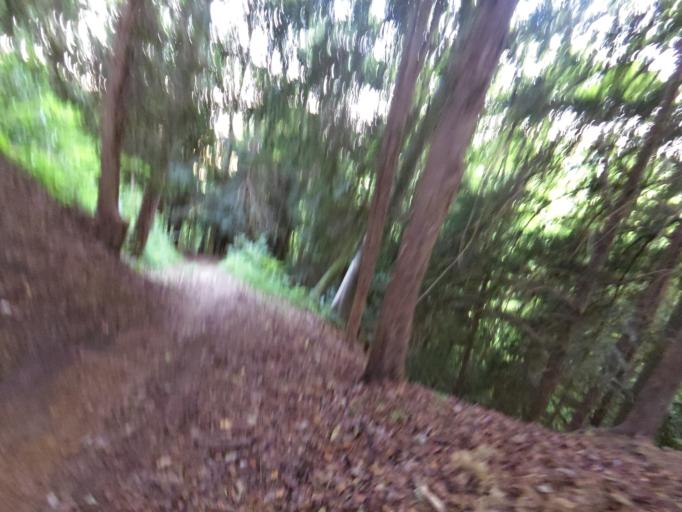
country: CH
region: Zurich
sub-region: Bezirk Zuerich
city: Zuerich (Kreis 2) / Mittel-Leimbach
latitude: 47.3289
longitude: 8.5050
